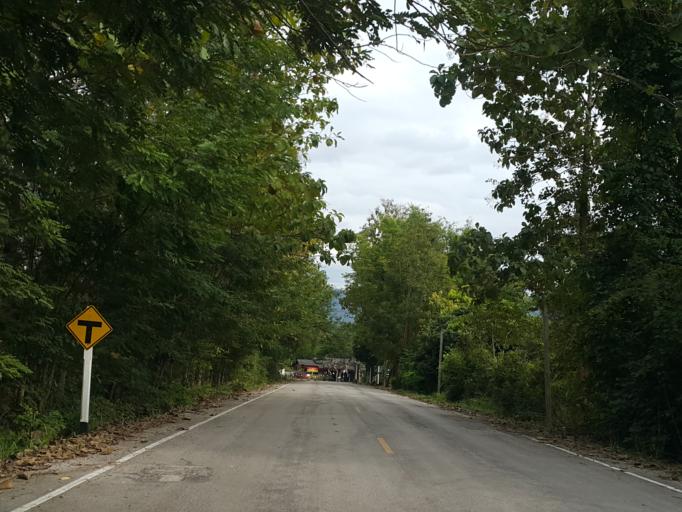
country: TH
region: Lampang
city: Chae Hom
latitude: 18.6528
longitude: 99.5356
